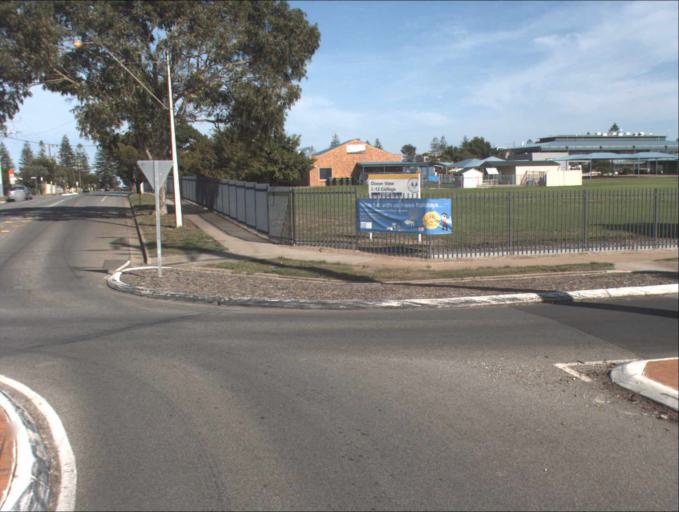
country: AU
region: South Australia
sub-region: Port Adelaide Enfield
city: Birkenhead
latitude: -34.8043
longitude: 138.4966
